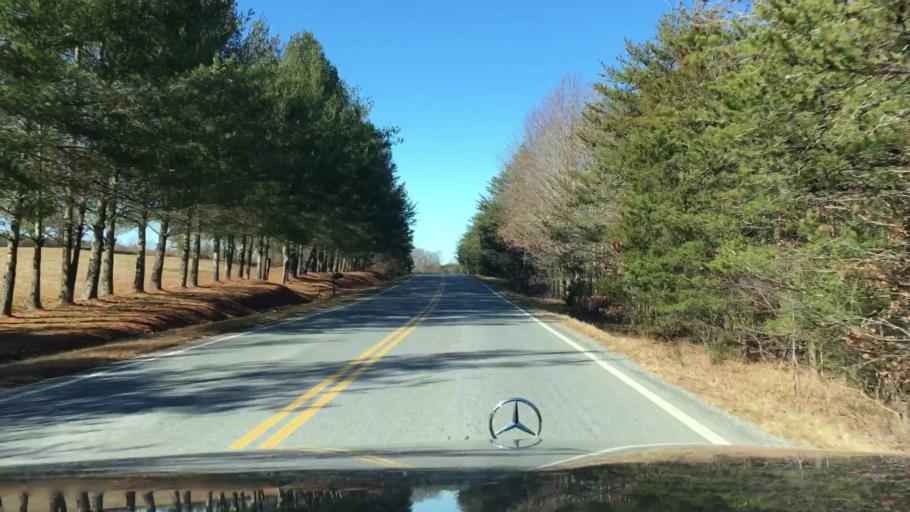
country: US
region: Virginia
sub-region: Pittsylvania County
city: Motley
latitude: 37.1786
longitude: -79.4091
